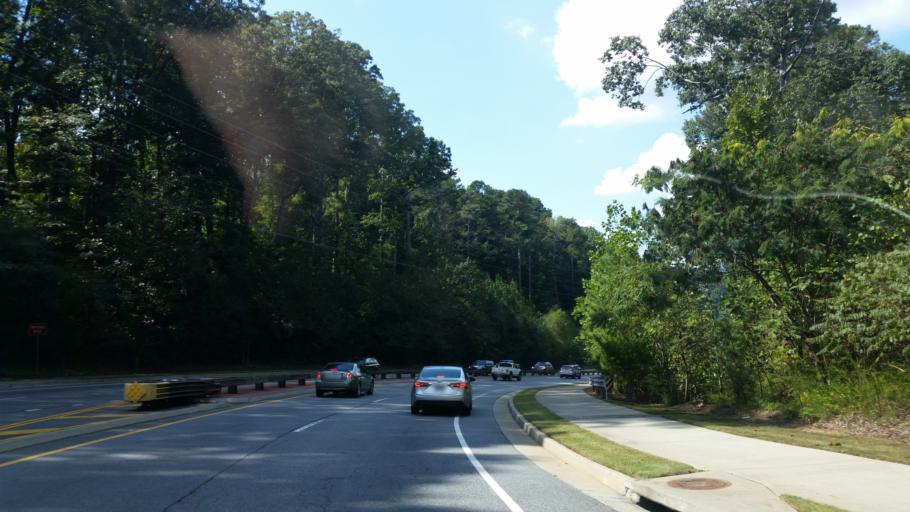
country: US
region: Georgia
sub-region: Fulton County
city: Sandy Springs
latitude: 33.9402
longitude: -84.4005
